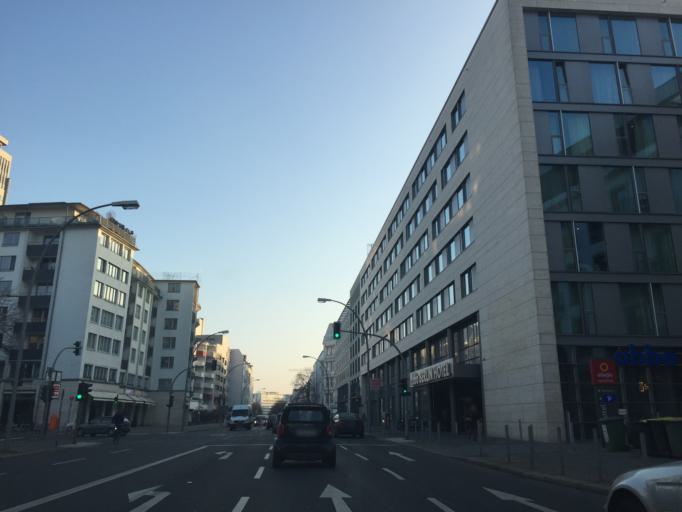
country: DE
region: Berlin
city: Wilmersdorf Bezirk
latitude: 52.4995
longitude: 13.3210
